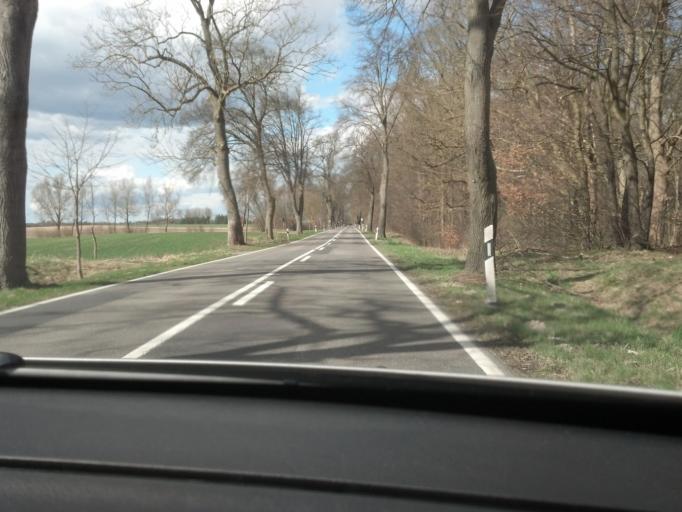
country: DE
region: Mecklenburg-Vorpommern
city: Burg Stargard
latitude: 53.4766
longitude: 13.3431
